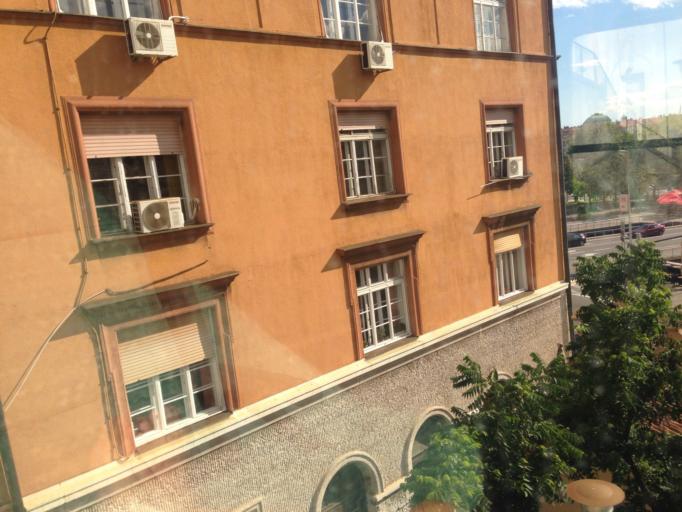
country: HR
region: Primorsko-Goranska
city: Drenova
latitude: 45.3280
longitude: 14.4491
